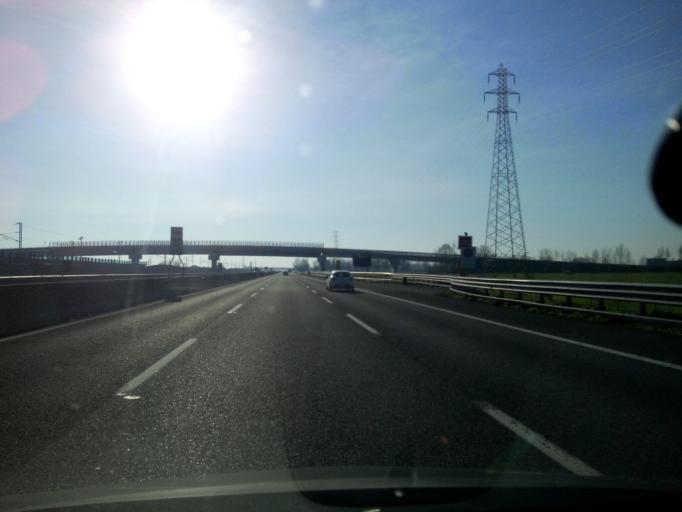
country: IT
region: Emilia-Romagna
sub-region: Provincia di Reggio Emilia
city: Prato
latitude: 44.6967
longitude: 10.7604
